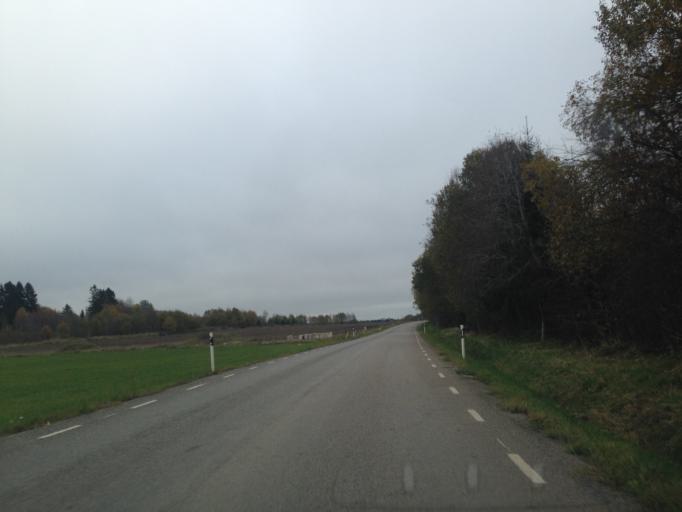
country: EE
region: Harju
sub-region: Saue linn
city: Saue
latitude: 59.3634
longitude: 24.5499
